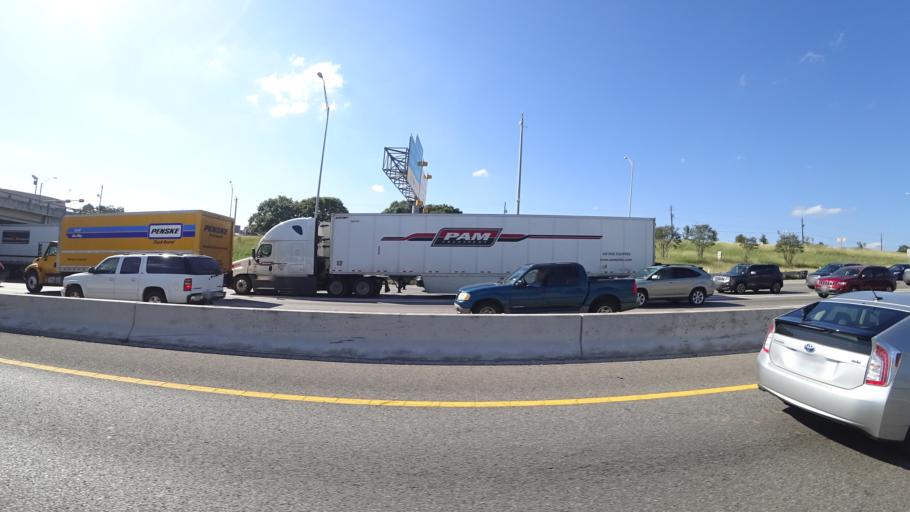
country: US
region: Texas
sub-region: Travis County
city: Austin
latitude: 30.2787
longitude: -97.7297
